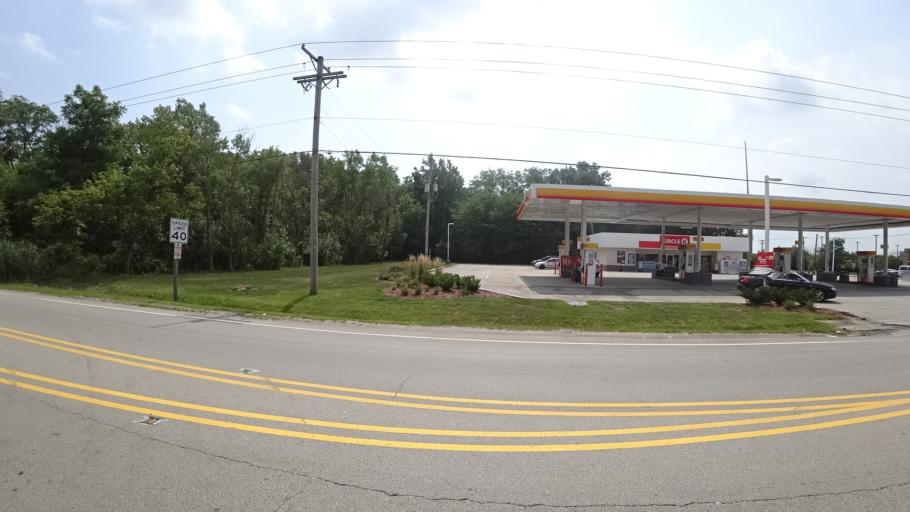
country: US
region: Illinois
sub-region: Cook County
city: Orland Park
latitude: 41.6298
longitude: -87.8916
